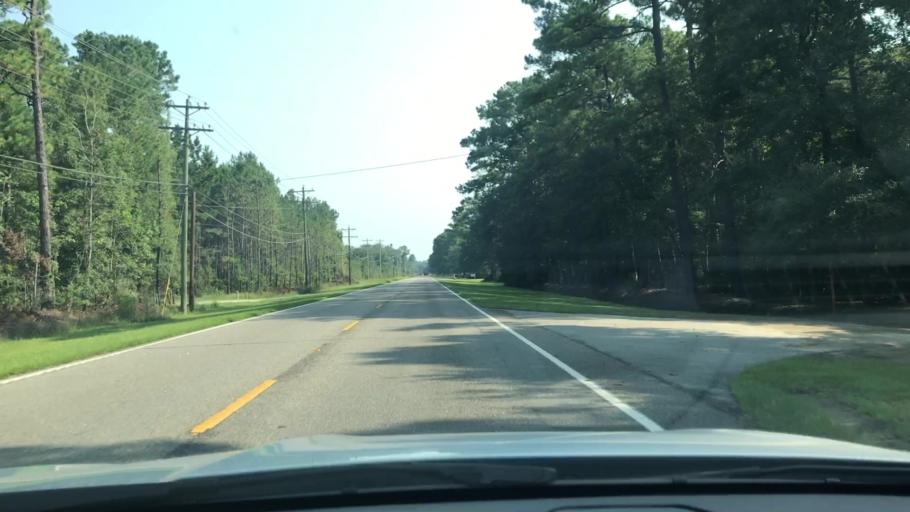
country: US
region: South Carolina
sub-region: Georgetown County
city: Georgetown
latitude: 33.4237
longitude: -79.2814
